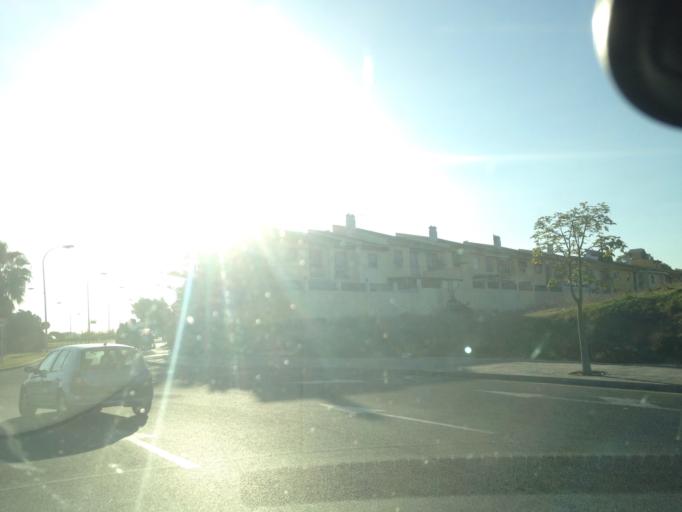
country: ES
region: Andalusia
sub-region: Provincia de Malaga
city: Malaga
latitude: 36.7082
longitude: -4.4824
